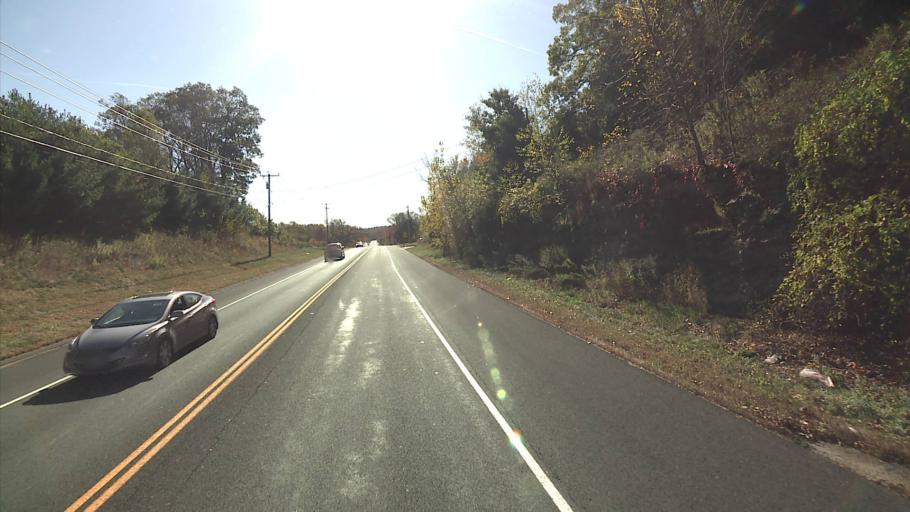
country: US
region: Connecticut
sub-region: Tolland County
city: Coventry Lake
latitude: 41.7590
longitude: -72.4023
